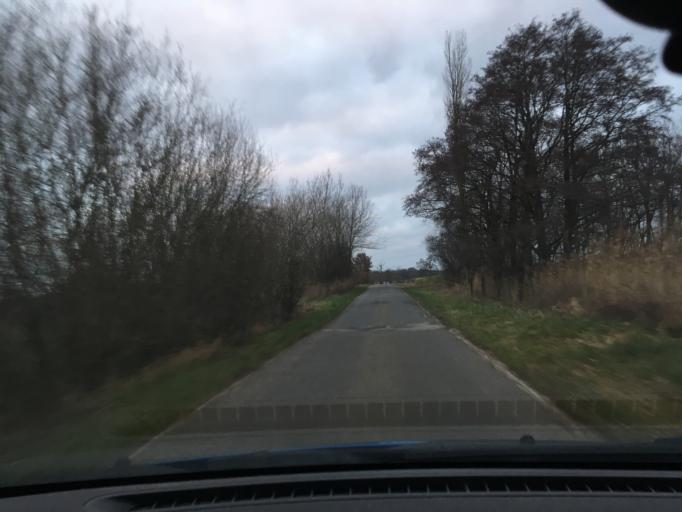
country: DE
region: Schleswig-Holstein
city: Kaaks
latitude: 54.0005
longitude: 9.4718
